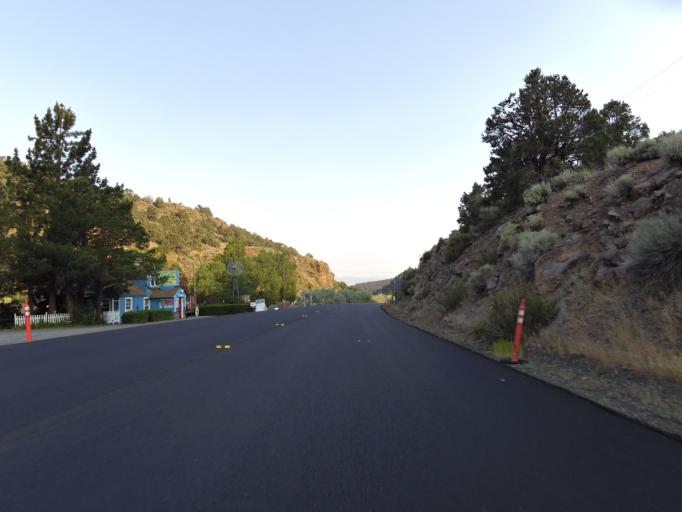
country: US
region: California
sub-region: Mono County
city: Bridgeport
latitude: 38.1868
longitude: -119.2032
